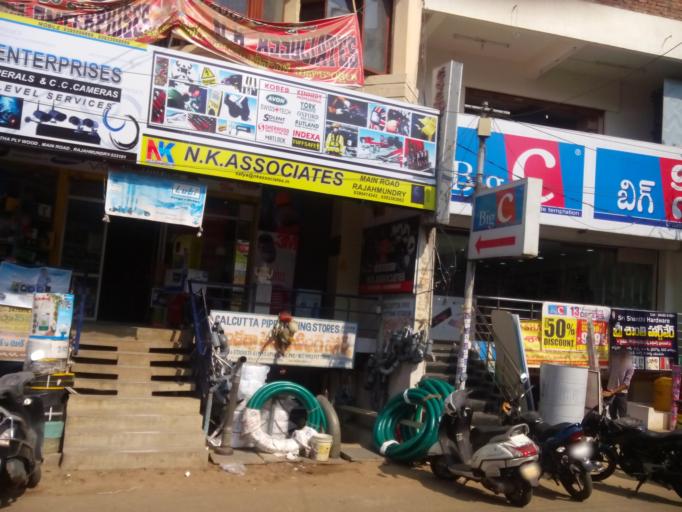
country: IN
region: Andhra Pradesh
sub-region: East Godavari
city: Rajahmundry
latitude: 16.9989
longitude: 81.7725
